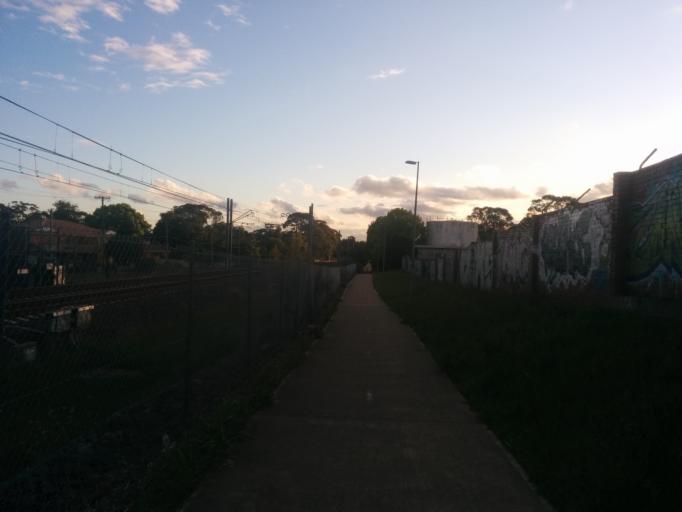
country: AU
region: New South Wales
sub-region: Fairfield
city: Fairfield East
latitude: -33.8673
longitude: 150.9660
